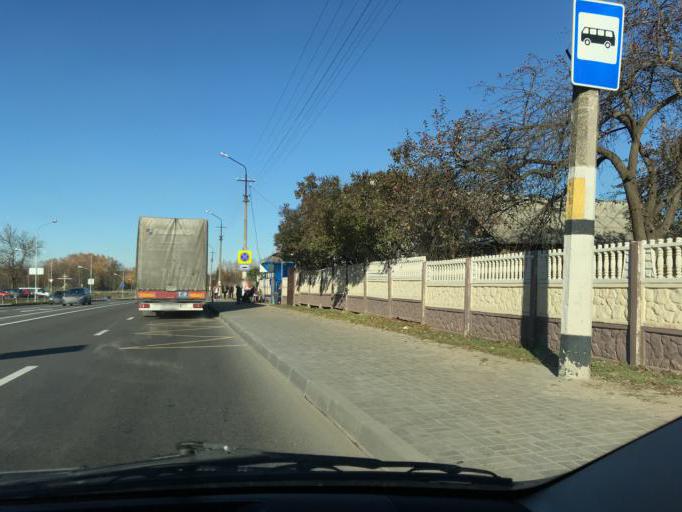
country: BY
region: Vitebsk
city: Polatsk
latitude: 55.5021
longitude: 28.7511
